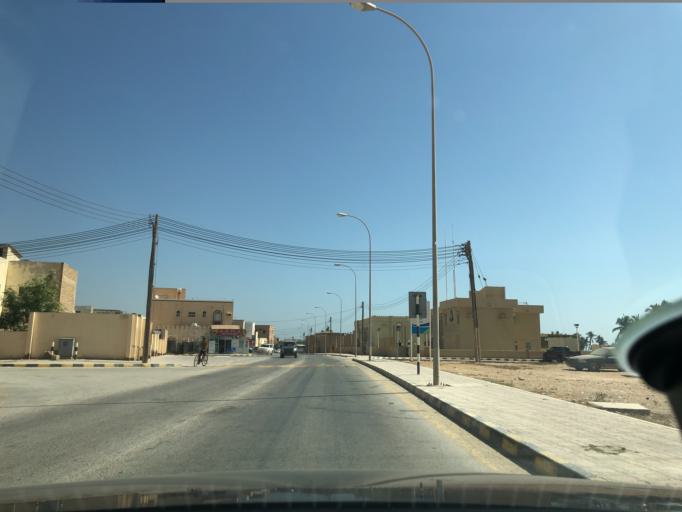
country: OM
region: Zufar
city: Salalah
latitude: 17.0384
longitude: 54.3916
